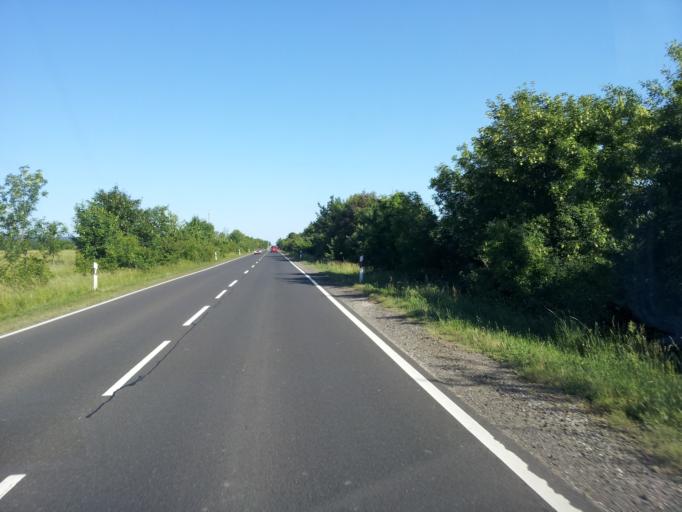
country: HU
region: Nograd
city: Nagyoroszi
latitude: 47.9870
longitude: 19.1119
